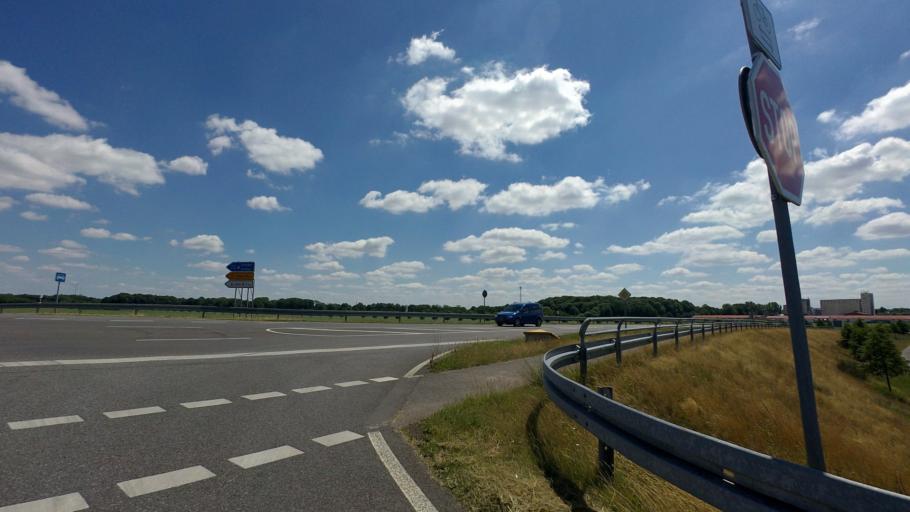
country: DE
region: Brandenburg
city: Luckau
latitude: 51.8641
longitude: 13.7024
